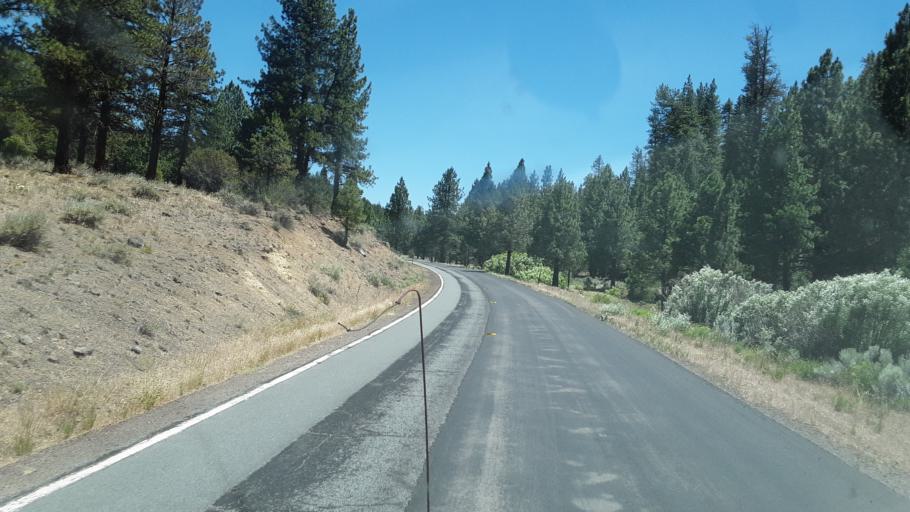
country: US
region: California
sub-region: Modoc County
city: Alturas
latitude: 41.0077
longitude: -120.8159
